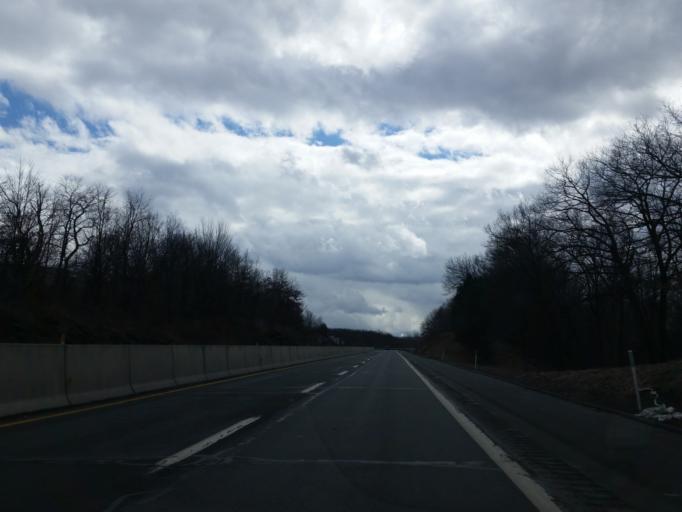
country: US
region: Pennsylvania
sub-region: Lackawanna County
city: Old Forge
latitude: 41.3663
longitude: -75.7195
